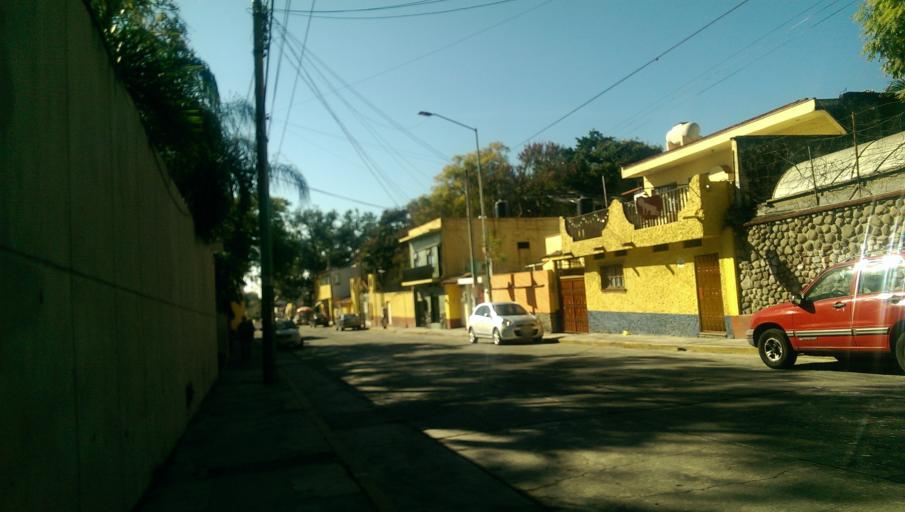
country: MX
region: Morelos
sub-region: Cuernavaca
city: Cuernavaca
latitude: 18.9213
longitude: -99.2416
